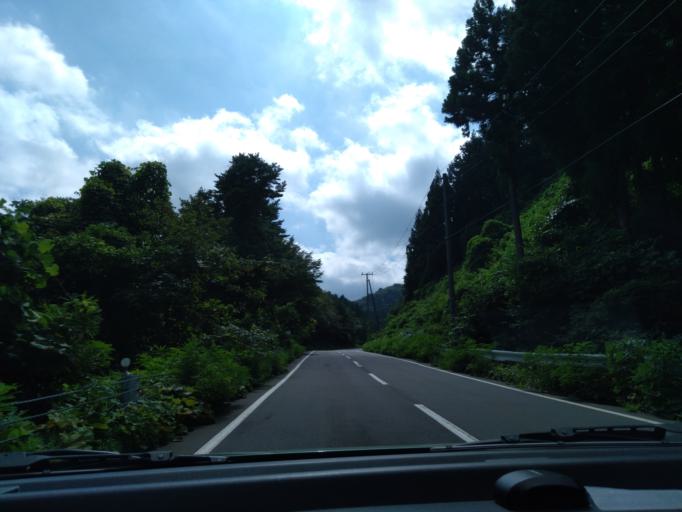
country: JP
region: Iwate
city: Morioka-shi
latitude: 39.6340
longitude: 141.0814
